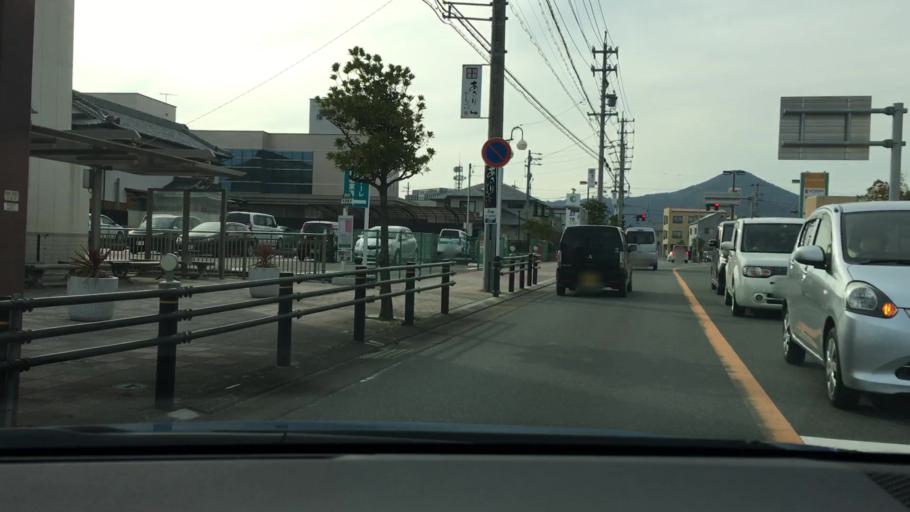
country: JP
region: Aichi
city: Tahara
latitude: 34.6689
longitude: 137.2691
